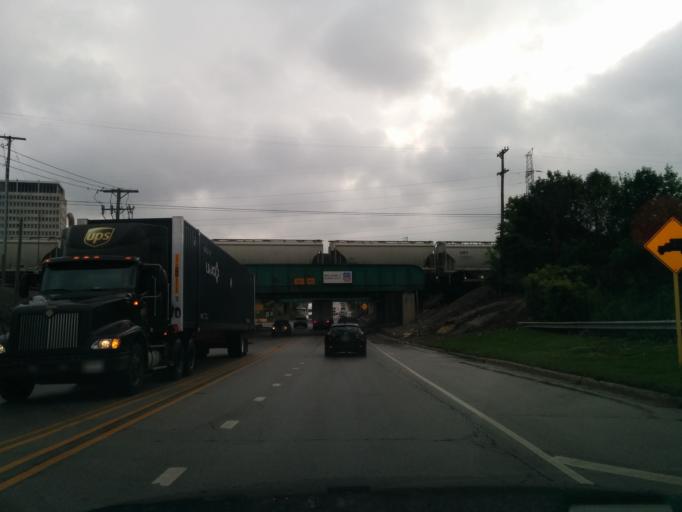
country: US
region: Illinois
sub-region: Cook County
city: Berkeley
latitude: 41.9055
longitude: -87.9146
